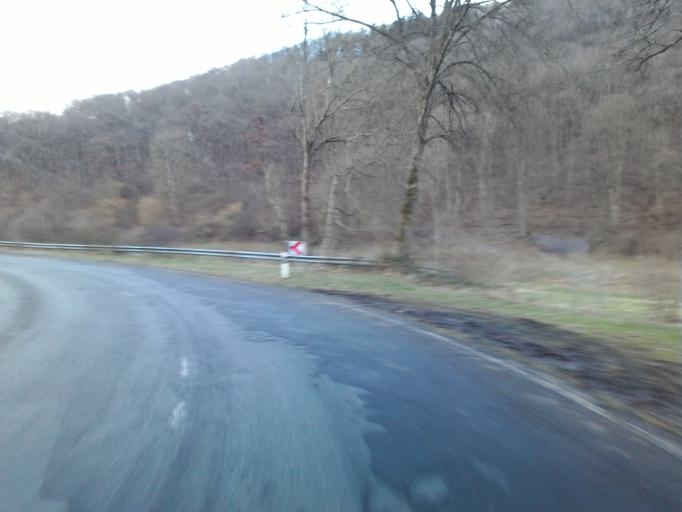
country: DE
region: Rheinland-Pfalz
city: Uppershausen
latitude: 50.0416
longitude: 6.3059
